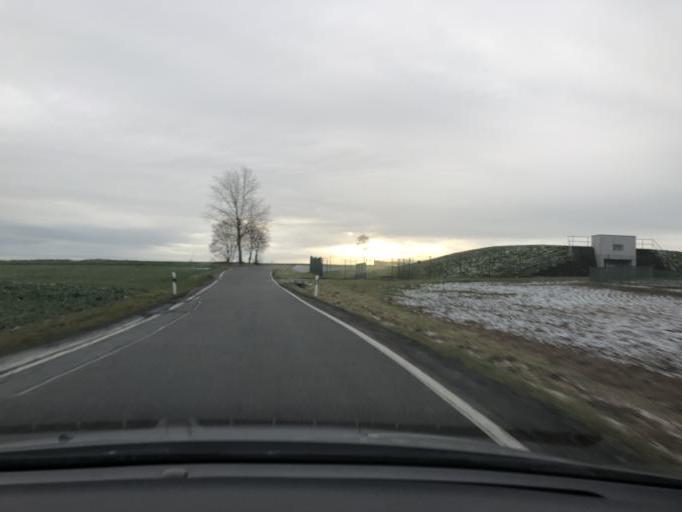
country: DE
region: Saxony
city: Niederfrohna
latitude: 50.8757
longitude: 12.7240
